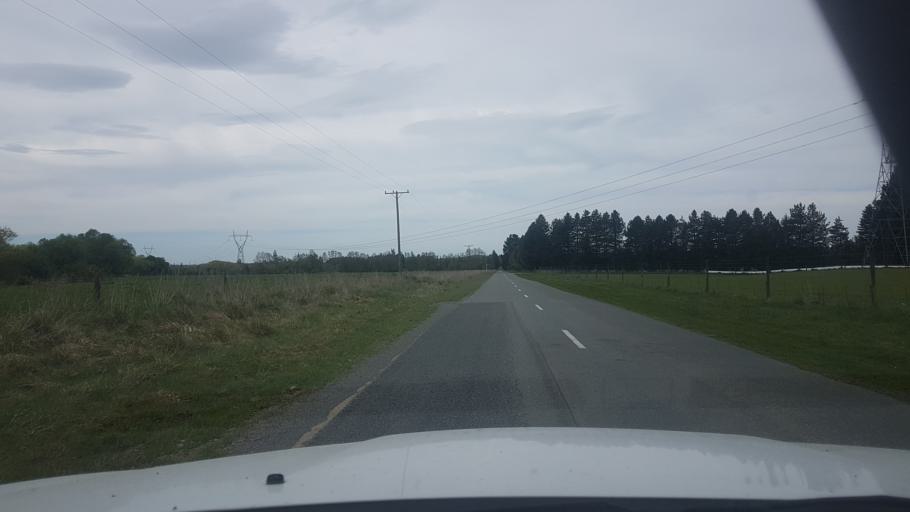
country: NZ
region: Canterbury
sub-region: Timaru District
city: Pleasant Point
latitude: -44.0715
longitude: 171.1481
